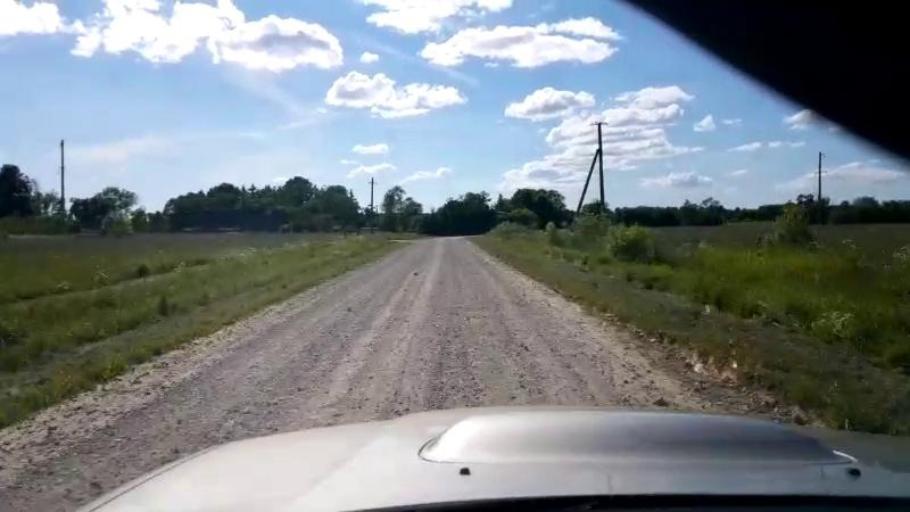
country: EE
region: Paernumaa
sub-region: Sauga vald
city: Sauga
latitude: 58.5090
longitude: 24.5523
